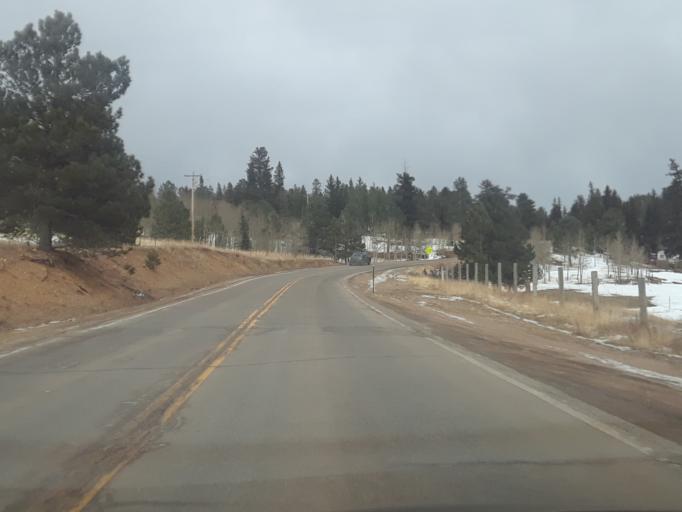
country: US
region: Colorado
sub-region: Boulder County
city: Coal Creek
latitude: 39.8181
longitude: -105.4008
